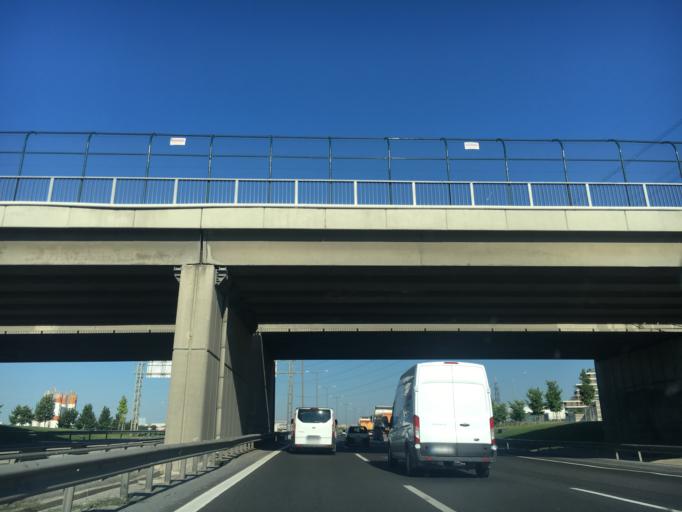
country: TR
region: Istanbul
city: Esenyurt
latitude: 41.0541
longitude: 28.6710
